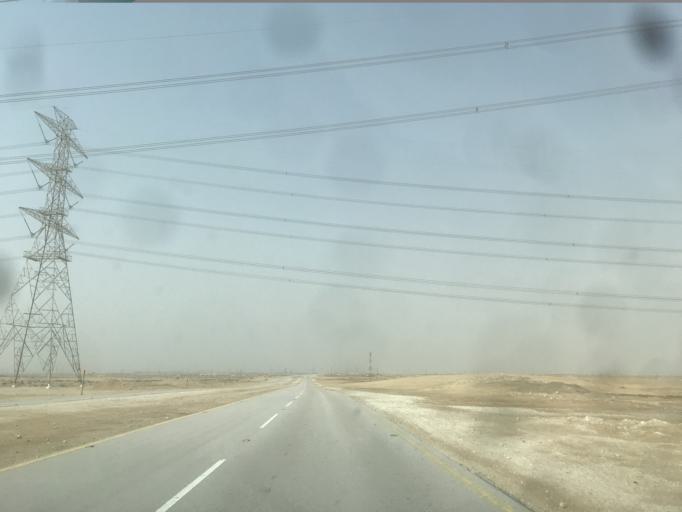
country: SA
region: Eastern Province
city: Abqaiq
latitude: 25.9283
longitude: 49.7537
